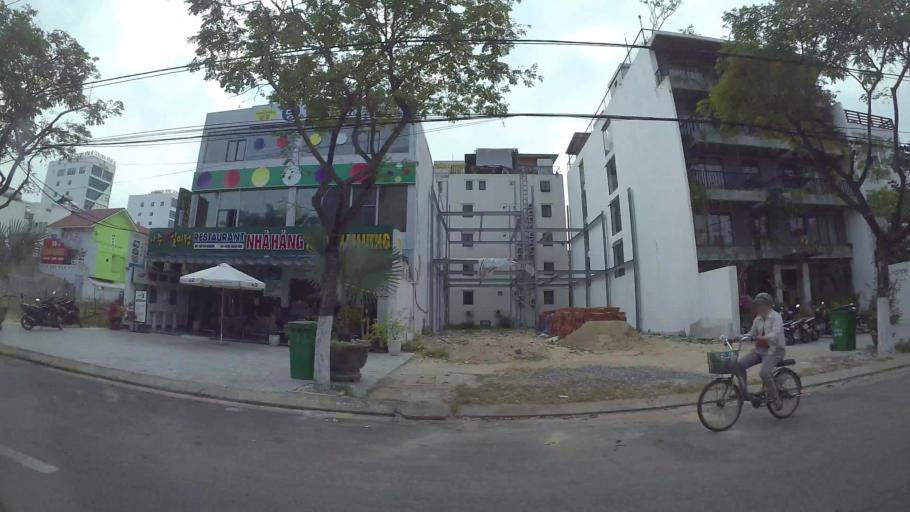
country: VN
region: Da Nang
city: Son Tra
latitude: 16.0744
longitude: 108.2429
